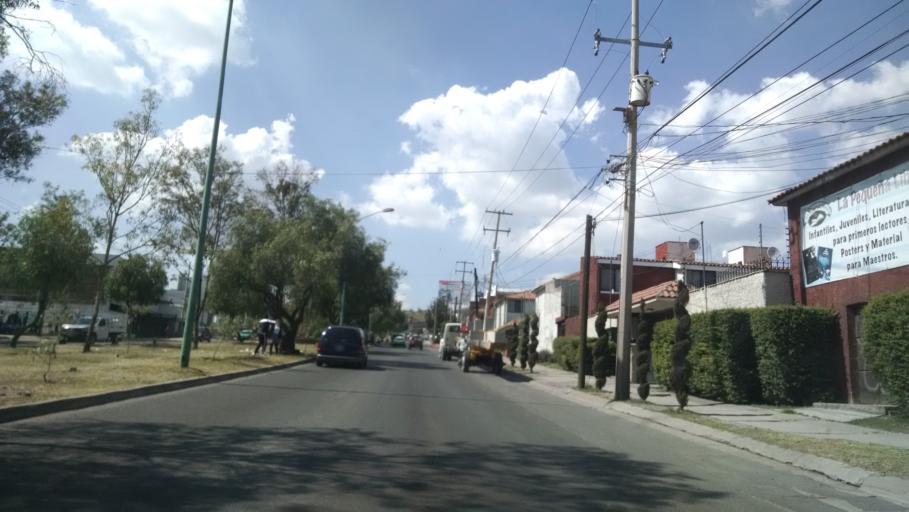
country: MX
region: Guanajuato
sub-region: Leon
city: Ejido la Joya
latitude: 21.1203
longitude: -101.7188
